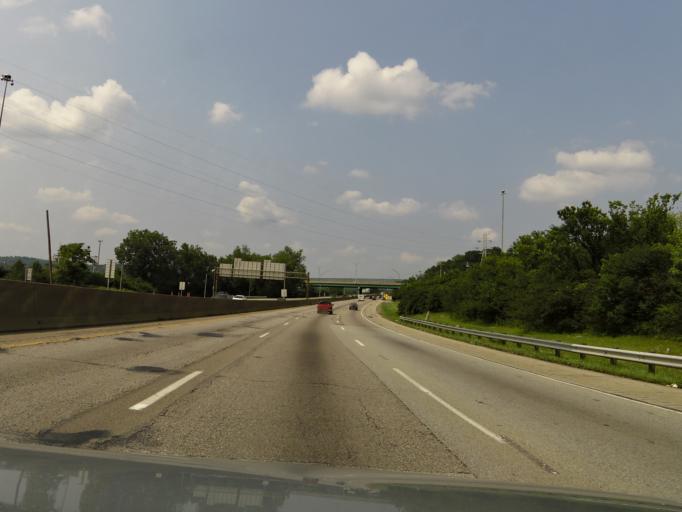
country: US
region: Ohio
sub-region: Hamilton County
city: Saint Bernard
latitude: 39.1519
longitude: -84.5398
